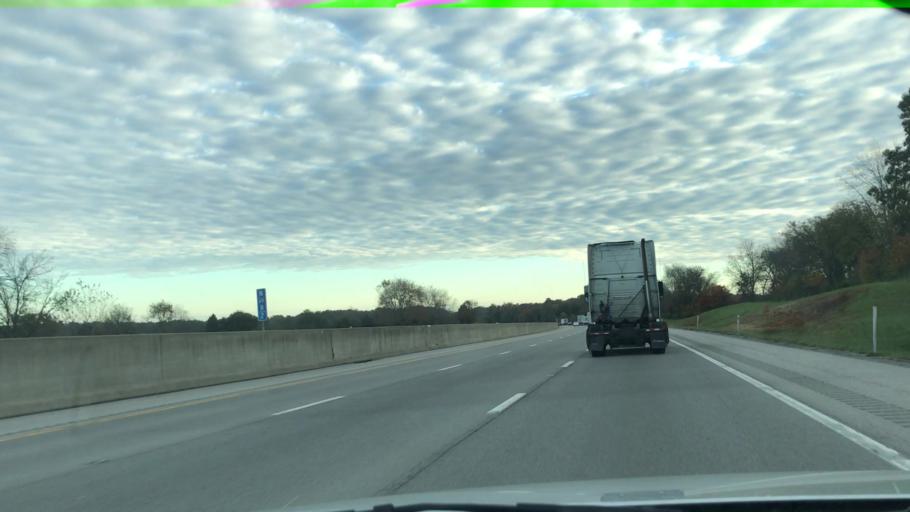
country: US
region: Kentucky
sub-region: Simpson County
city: Franklin
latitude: 36.7415
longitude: -86.5003
